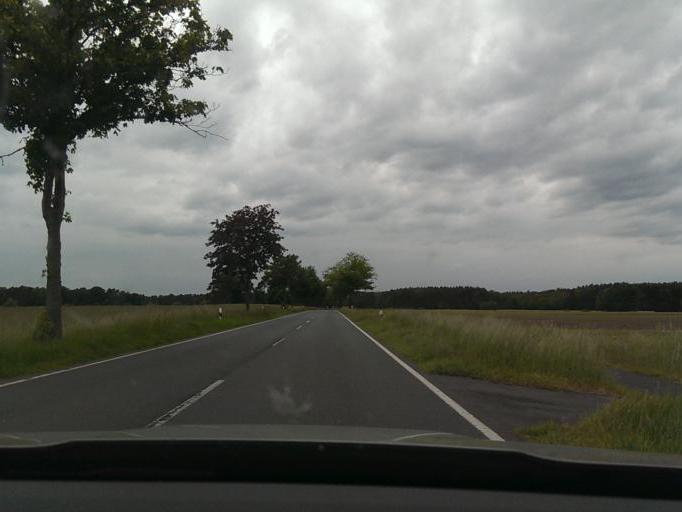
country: DE
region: Lower Saxony
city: Winsen (Aller)
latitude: 52.6817
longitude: 9.8824
